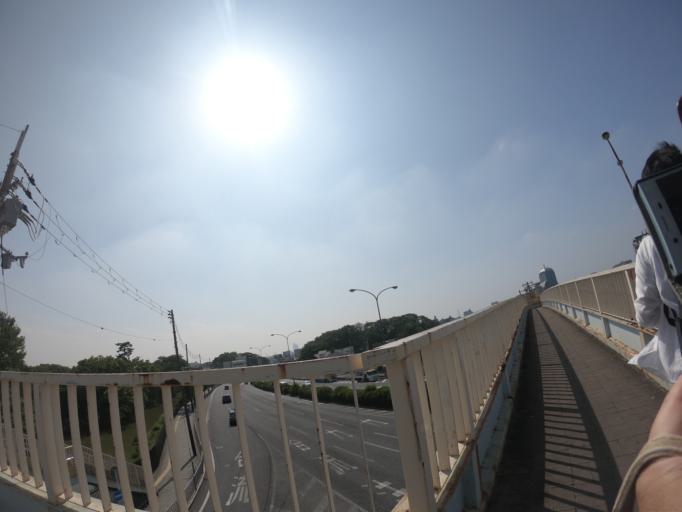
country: JP
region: Osaka
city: Sakai
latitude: 34.5677
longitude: 135.4890
